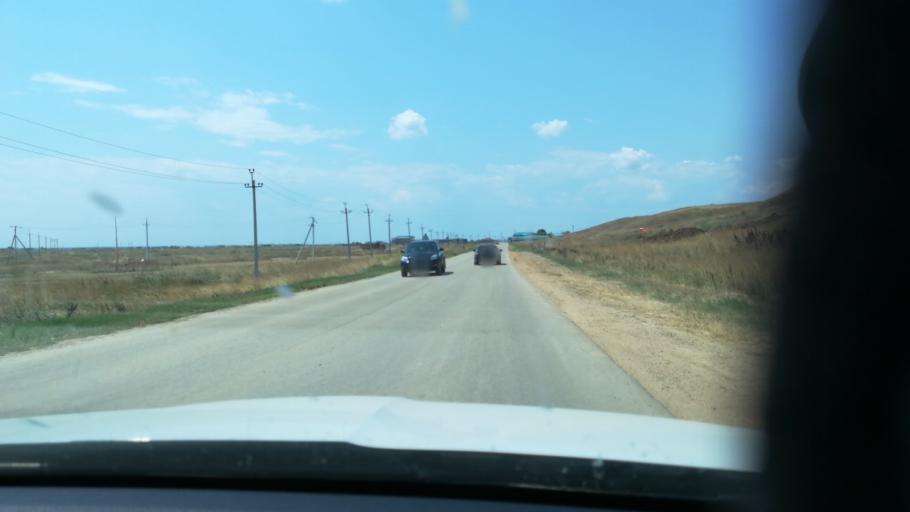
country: RU
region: Krasnodarskiy
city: Vyshestebliyevskaya
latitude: 45.1159
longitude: 36.8926
